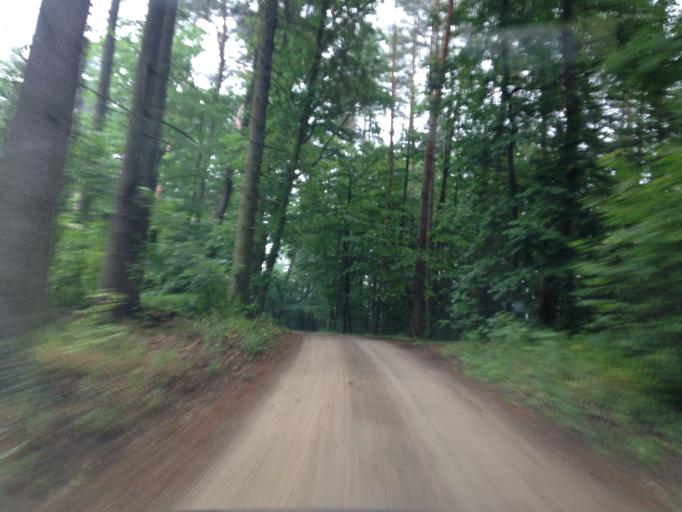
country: PL
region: Kujawsko-Pomorskie
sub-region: Powiat brodnicki
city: Brodnica
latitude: 53.3222
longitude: 19.3522
